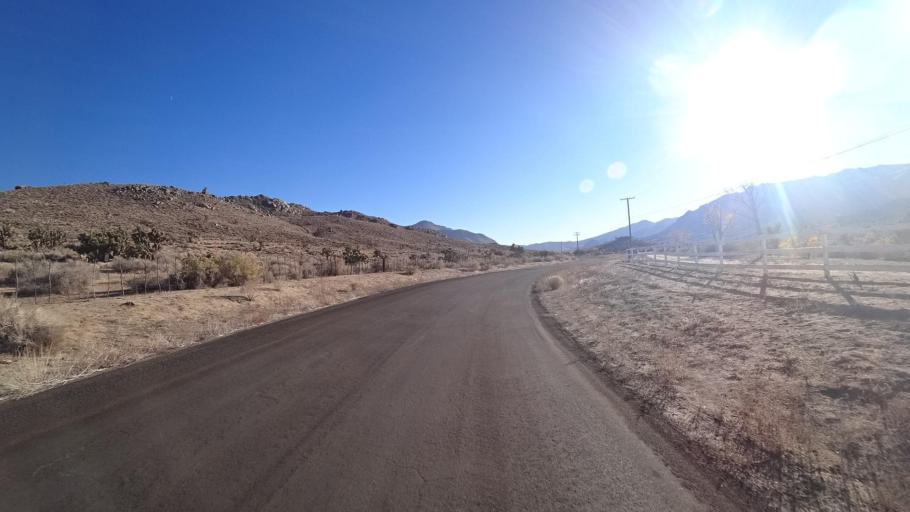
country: US
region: California
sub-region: Kern County
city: Weldon
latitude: 35.5119
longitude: -118.2027
